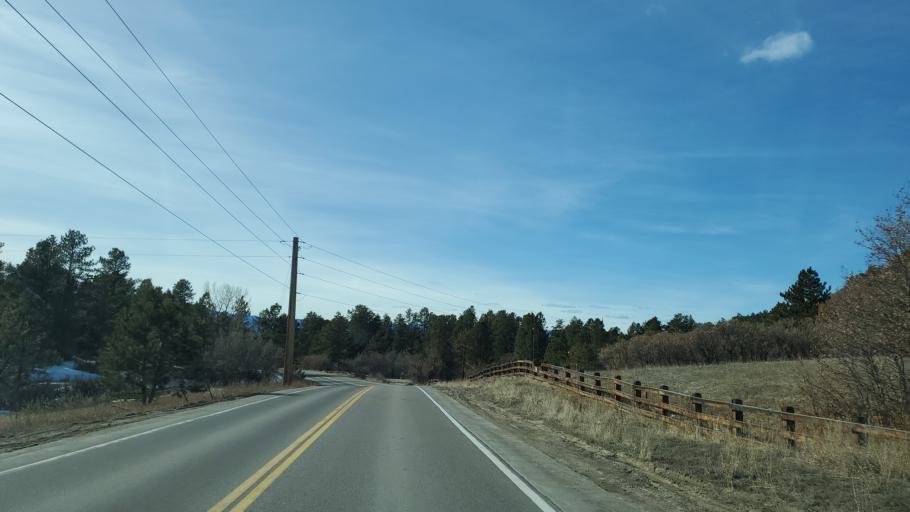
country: US
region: Colorado
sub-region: Douglas County
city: Castle Pines
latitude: 39.4447
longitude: -104.8813
